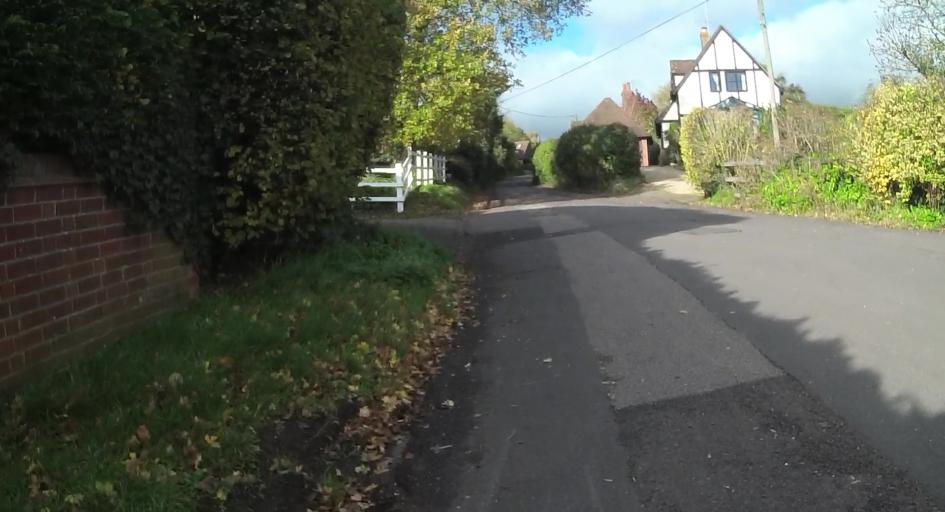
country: GB
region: England
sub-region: Hampshire
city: Old Basing
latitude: 51.2820
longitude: -1.0494
